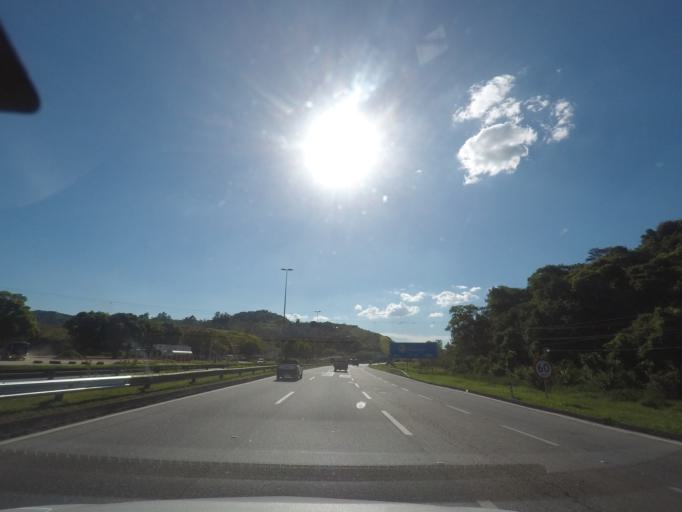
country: BR
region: Rio de Janeiro
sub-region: Petropolis
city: Petropolis
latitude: -22.6571
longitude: -43.1292
